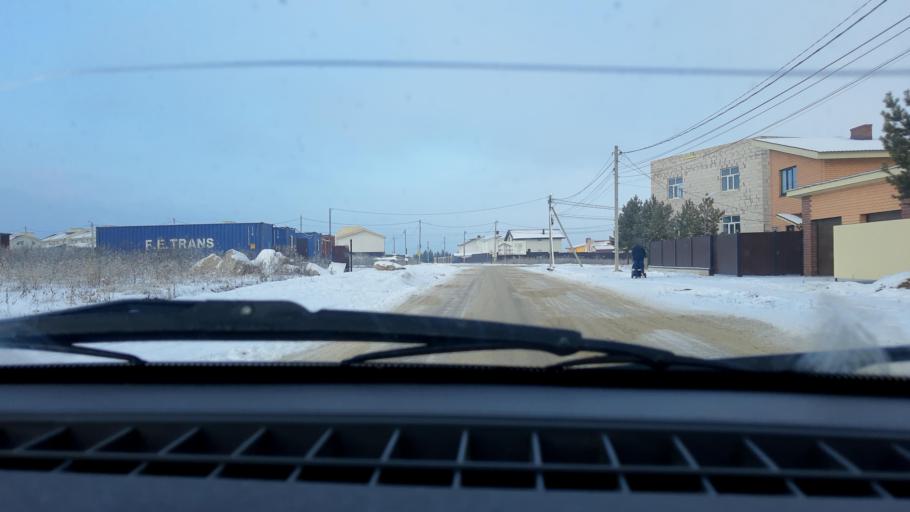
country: RU
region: Bashkortostan
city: Avdon
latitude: 54.4793
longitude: 55.8759
